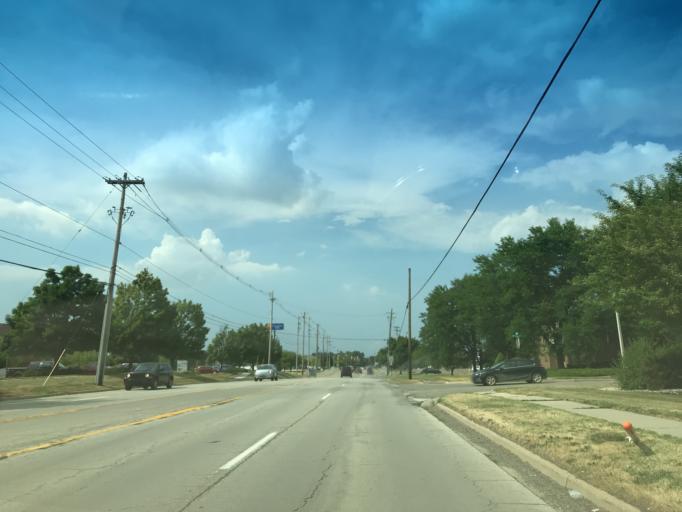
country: US
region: Michigan
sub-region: Eaton County
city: Waverly
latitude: 42.7377
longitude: -84.6619
